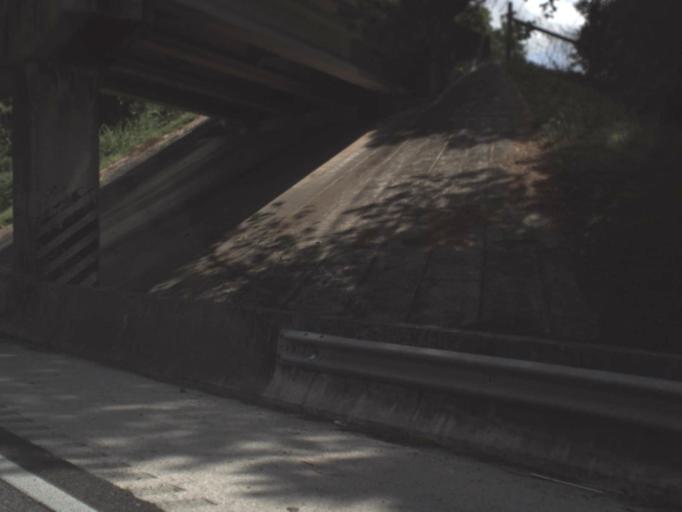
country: US
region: Florida
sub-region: Alachua County
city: High Springs
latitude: 29.8388
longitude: -82.5278
